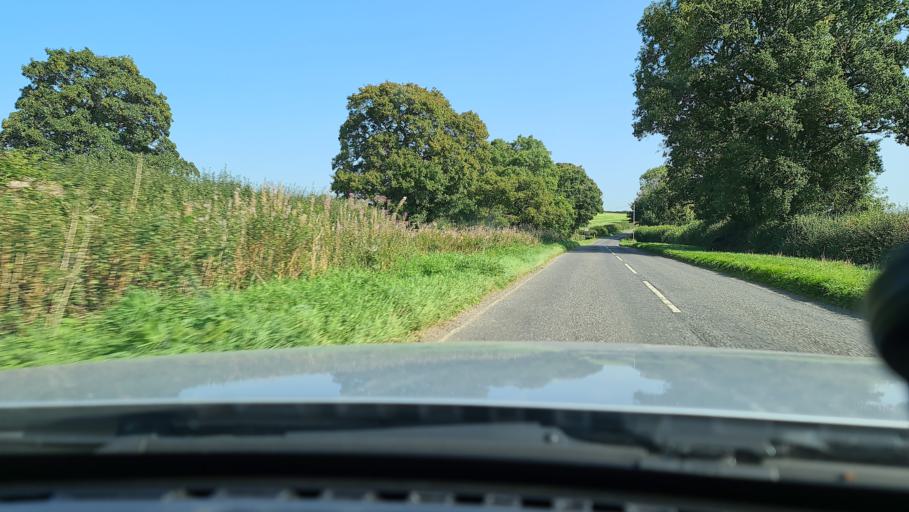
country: GB
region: England
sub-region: Northamptonshire
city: Bugbrooke
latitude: 52.1735
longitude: -1.1003
